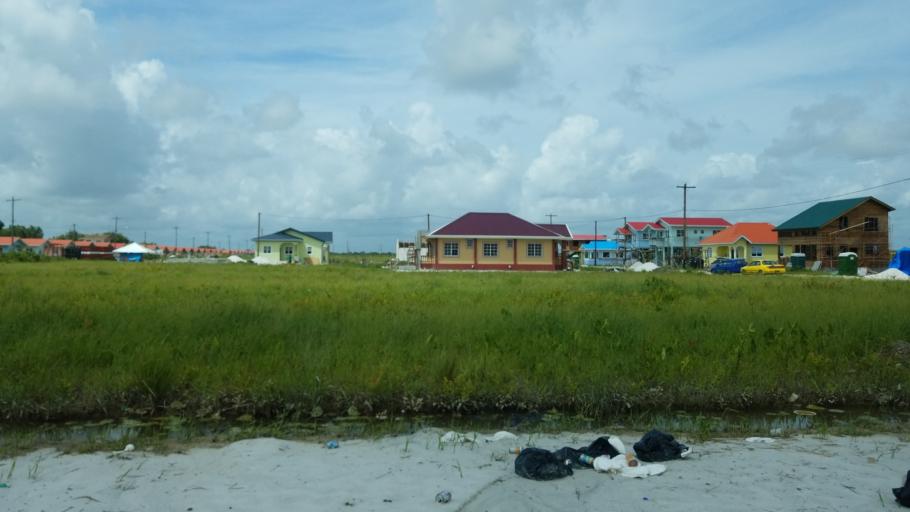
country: GY
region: Demerara-Mahaica
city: Georgetown
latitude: 6.7527
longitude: -58.1453
